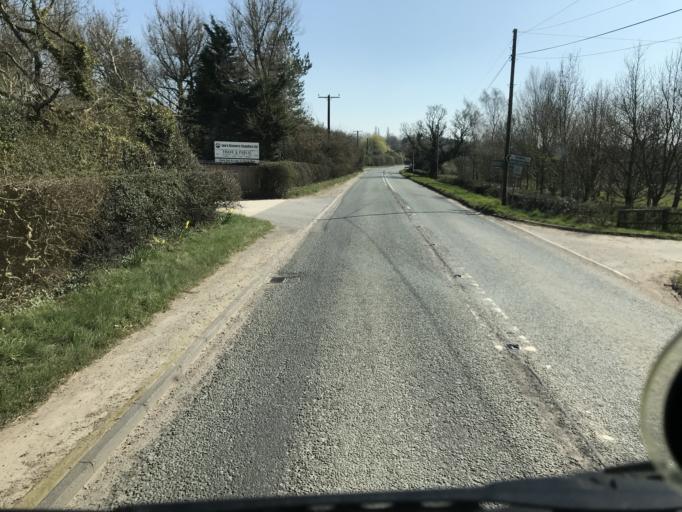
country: GB
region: England
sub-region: Cheshire East
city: Mobberley
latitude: 53.2813
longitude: -2.3123
